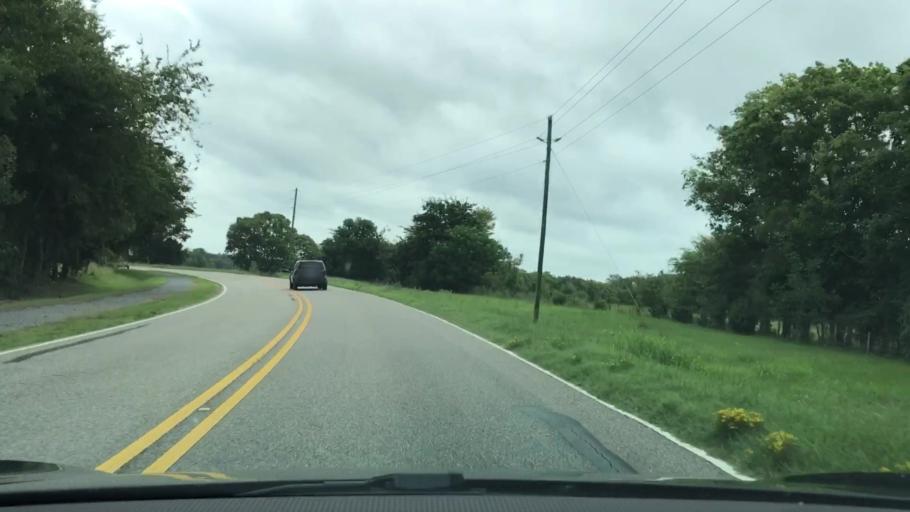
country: US
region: Alabama
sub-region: Montgomery County
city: Pike Road
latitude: 32.3029
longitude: -86.0511
